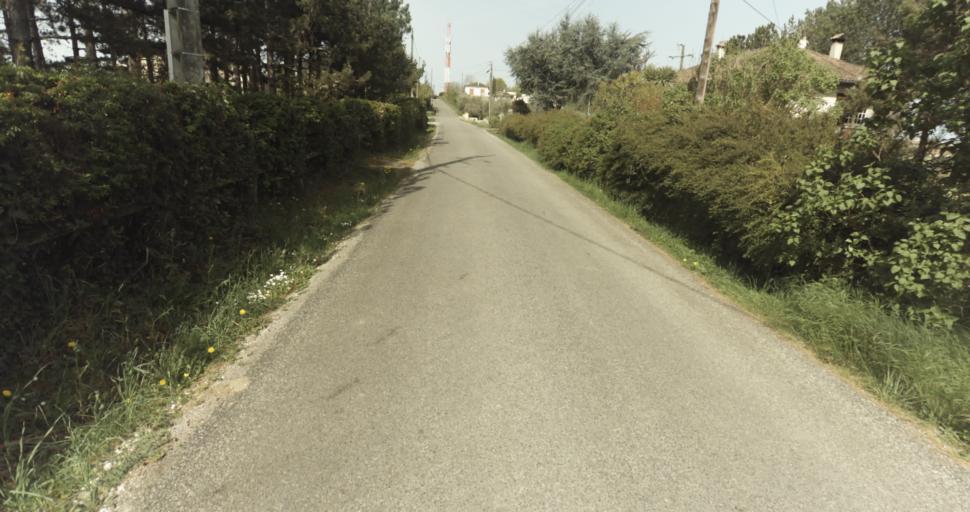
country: FR
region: Midi-Pyrenees
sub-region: Departement du Tarn-et-Garonne
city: Moissac
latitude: 44.1079
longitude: 1.0752
